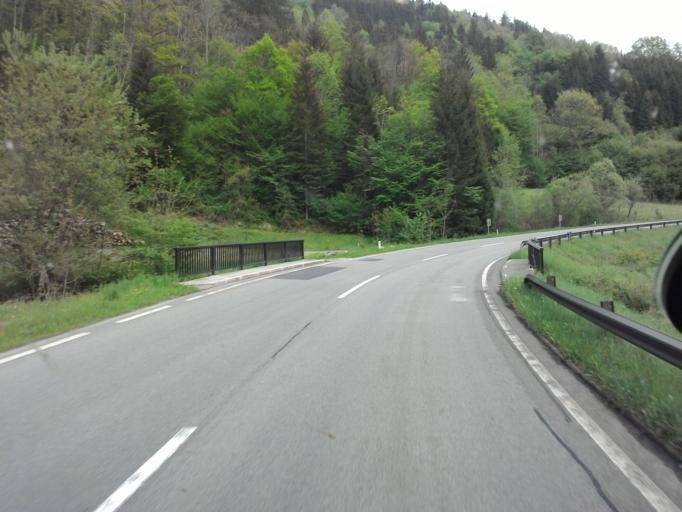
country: AT
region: Styria
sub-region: Politischer Bezirk Liezen
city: Altenmarkt bei Sankt Gallen
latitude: 47.7235
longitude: 14.6696
